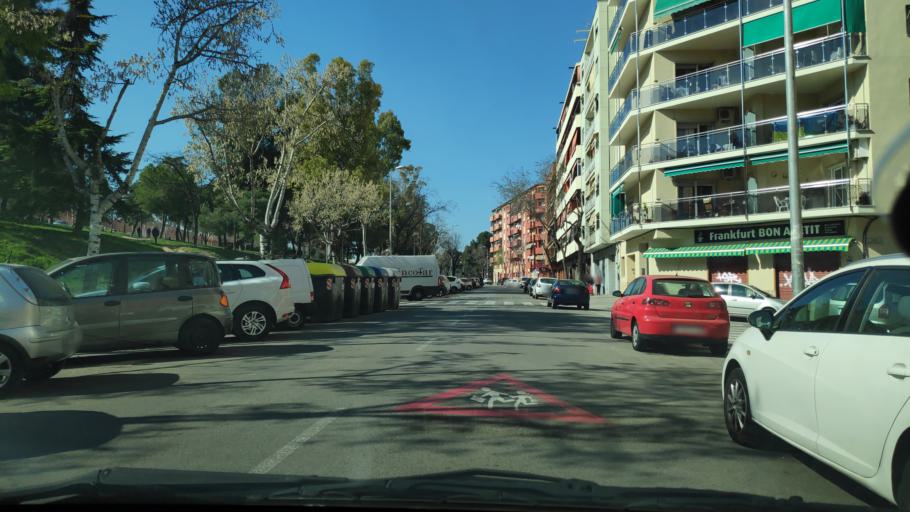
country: ES
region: Catalonia
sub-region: Provincia de Barcelona
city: Sabadell
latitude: 41.5580
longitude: 2.0934
